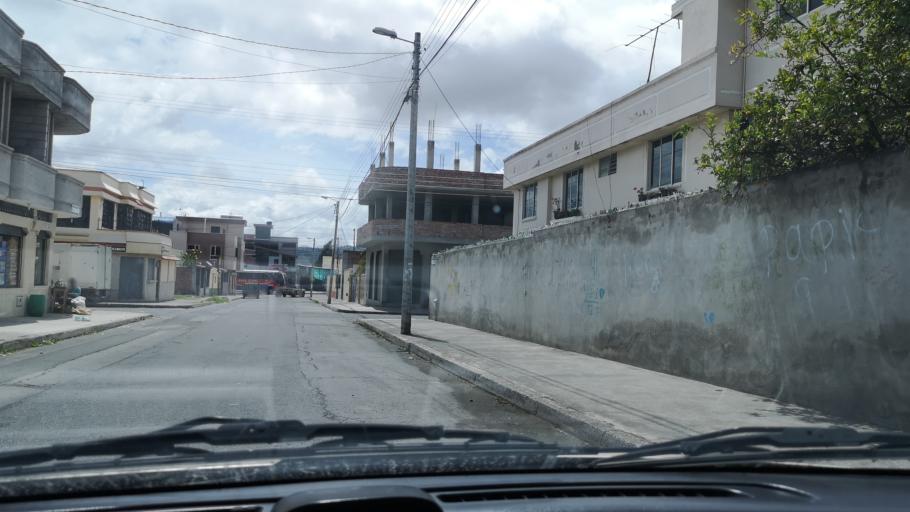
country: EC
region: Chimborazo
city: Riobamba
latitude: -1.6459
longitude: -78.6833
